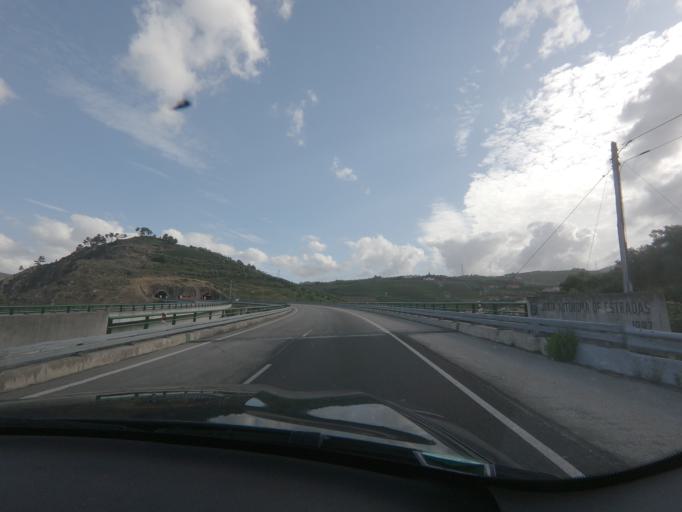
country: PT
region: Vila Real
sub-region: Peso da Regua
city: Peso da Regua
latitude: 41.1260
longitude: -7.7794
